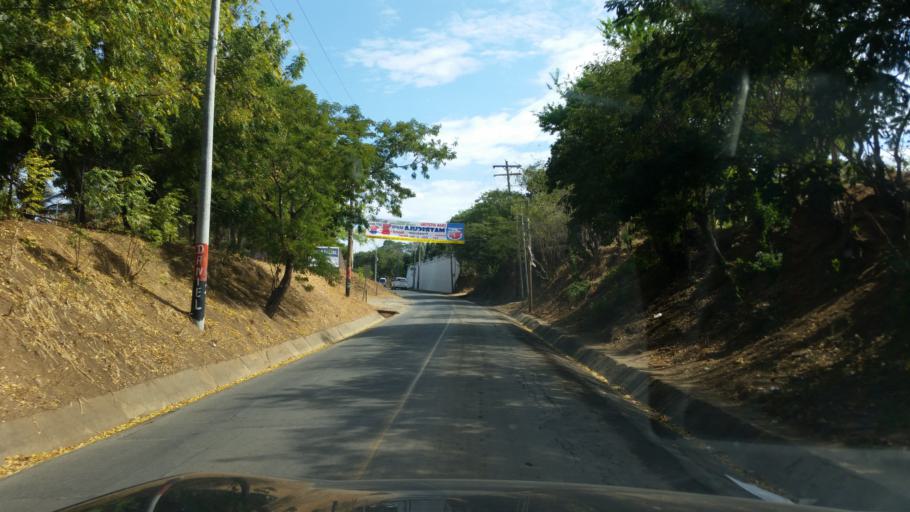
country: NI
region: Managua
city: Managua
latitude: 12.1001
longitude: -86.2495
